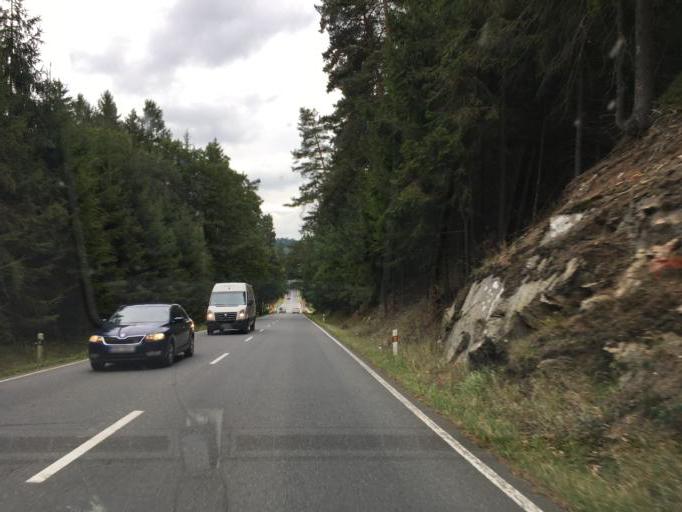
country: CZ
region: Vysocina
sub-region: Okres Pelhrimov
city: Pelhrimov
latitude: 49.4745
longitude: 15.1834
